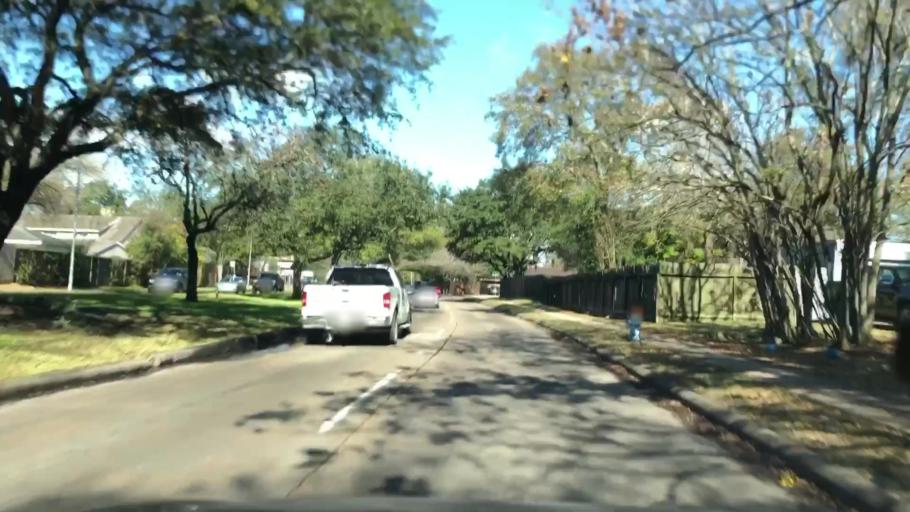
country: US
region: Texas
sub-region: Harris County
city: Bellaire
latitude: 29.6718
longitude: -95.4923
